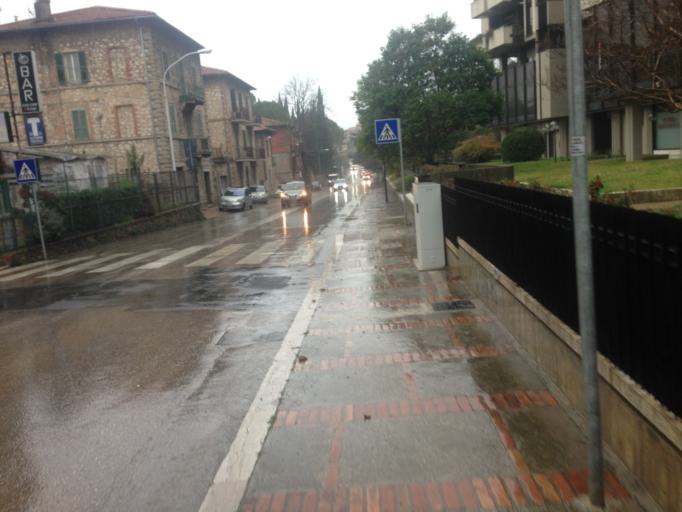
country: IT
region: Umbria
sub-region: Provincia di Perugia
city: Perugia
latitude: 43.1043
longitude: 12.3738
